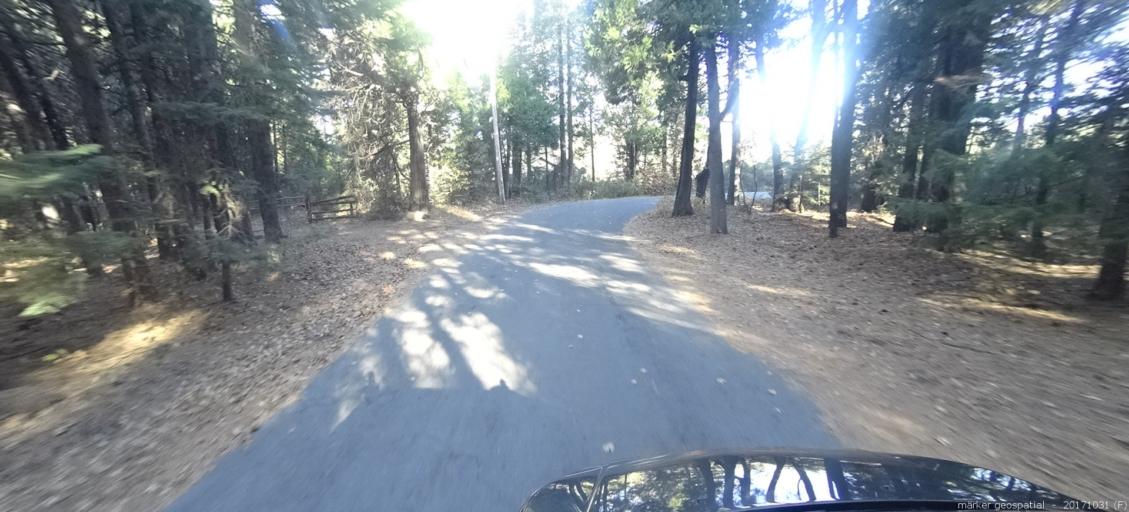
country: US
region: California
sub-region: Shasta County
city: Shingletown
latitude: 40.5210
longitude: -121.8394
